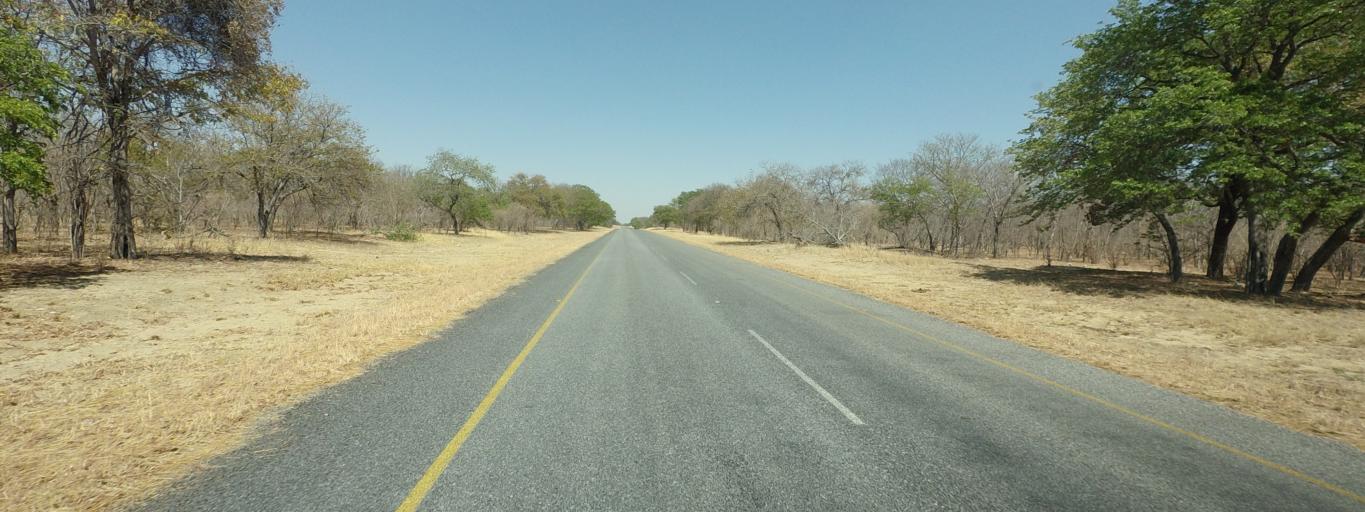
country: BW
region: North West
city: Kasane
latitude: -17.9280
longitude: 24.7428
